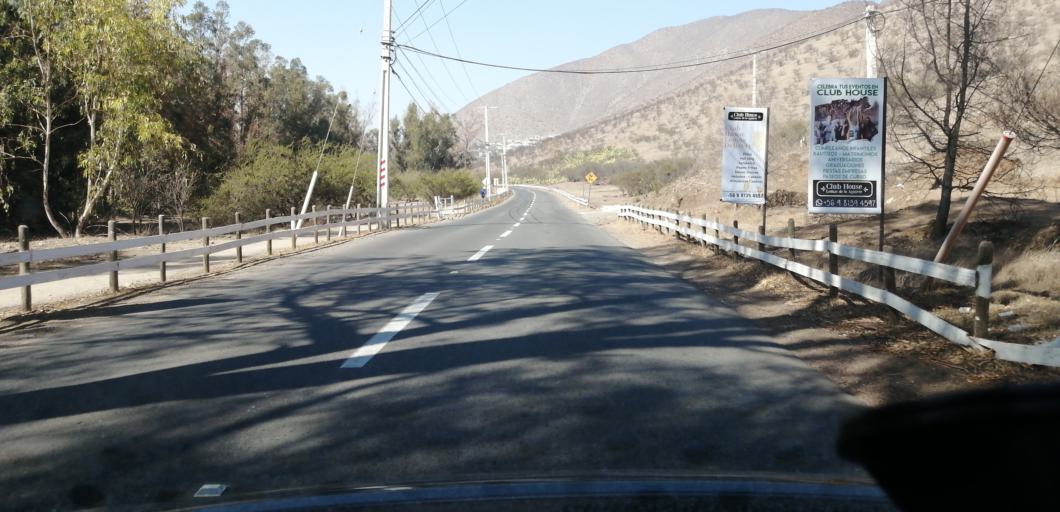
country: CL
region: Santiago Metropolitan
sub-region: Provincia de Santiago
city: Lo Prado
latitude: -33.4406
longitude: -70.8261
